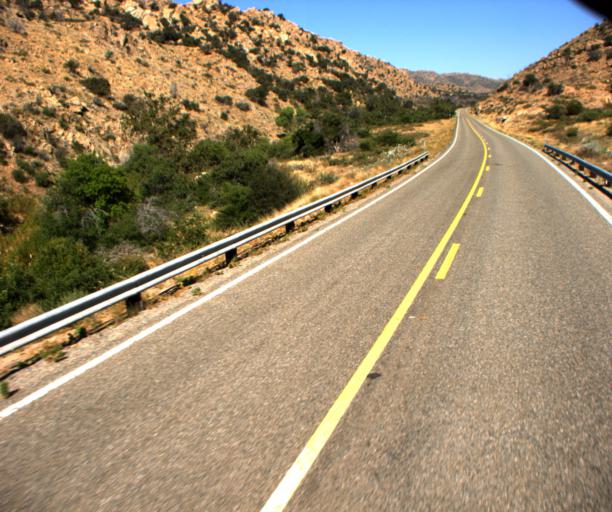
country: US
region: Arizona
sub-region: Graham County
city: Swift Trail Junction
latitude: 32.5620
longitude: -109.7917
